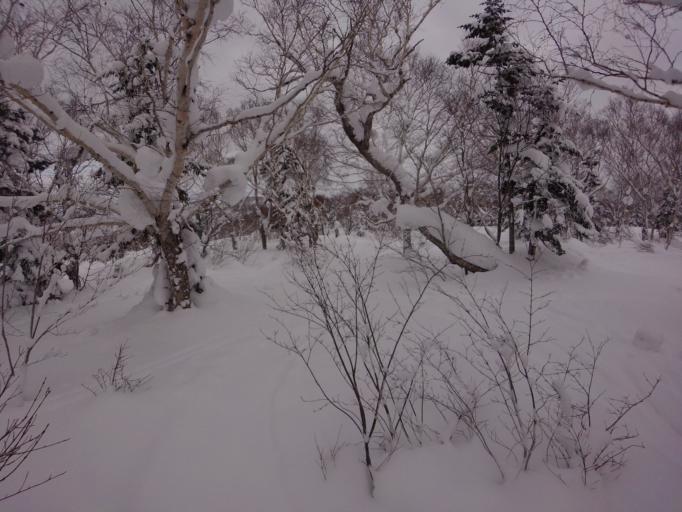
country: JP
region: Hokkaido
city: Sapporo
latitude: 43.0753
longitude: 141.2016
